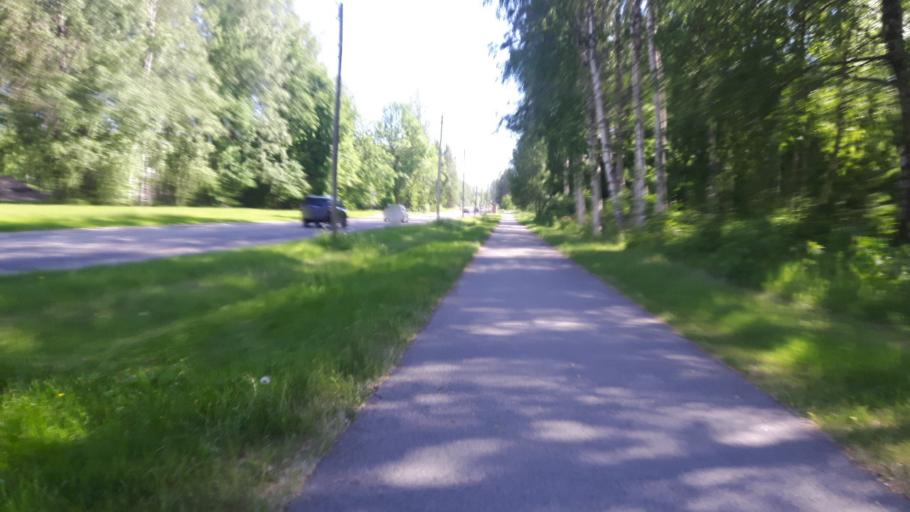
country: EE
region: Paernumaa
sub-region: Paikuse vald
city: Paikuse
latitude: 58.3942
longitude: 24.6408
